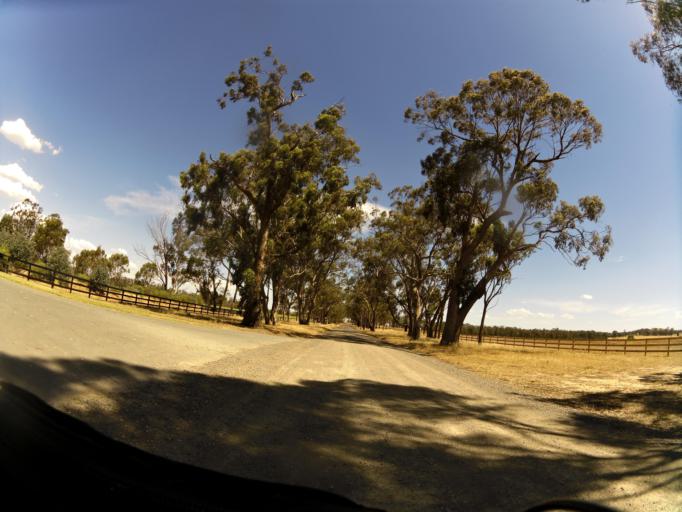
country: AU
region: Victoria
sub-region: Campaspe
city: Kyabram
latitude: -36.8347
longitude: 145.0744
